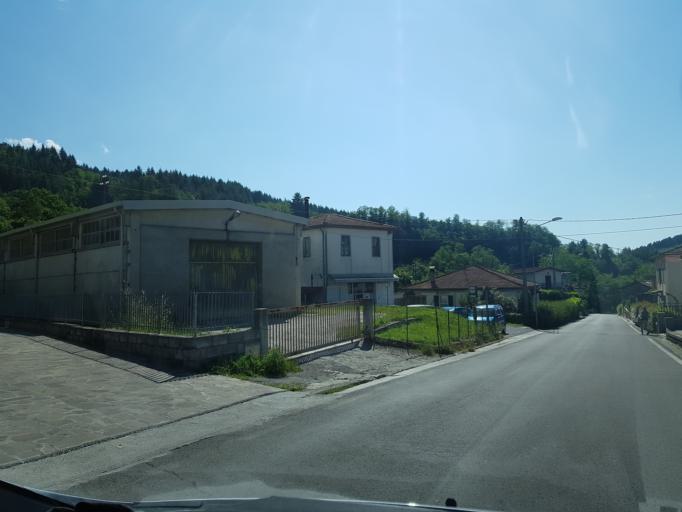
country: IT
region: Tuscany
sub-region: Provincia di Lucca
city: Piazza al Serchio-San Michele
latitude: 44.1747
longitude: 10.3131
